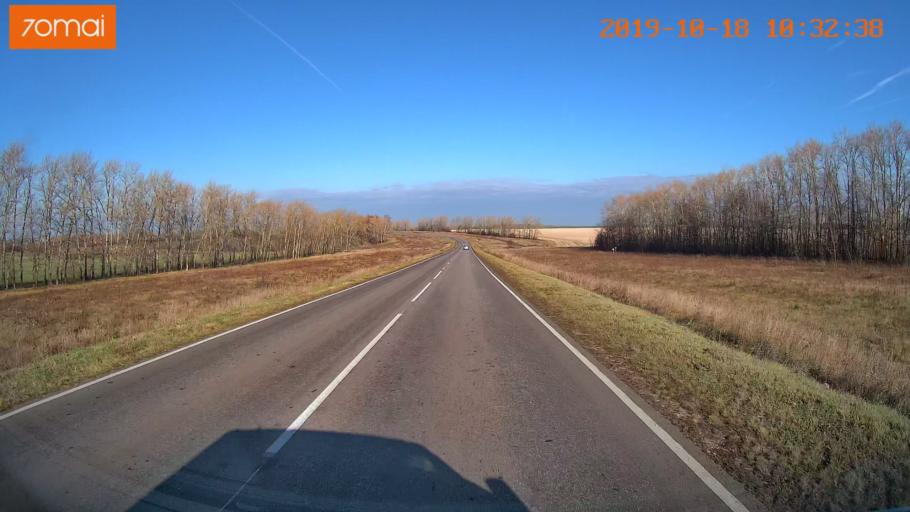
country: RU
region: Tula
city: Kurkino
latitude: 53.4969
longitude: 38.6209
